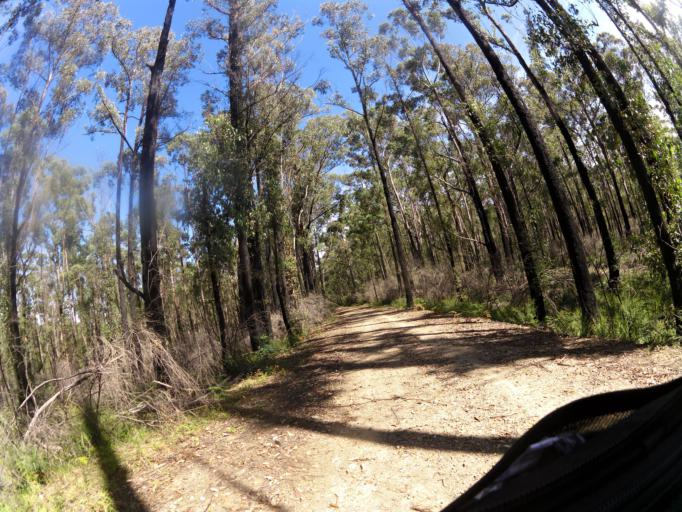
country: AU
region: Victoria
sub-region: East Gippsland
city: Lakes Entrance
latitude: -37.7264
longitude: 148.1600
